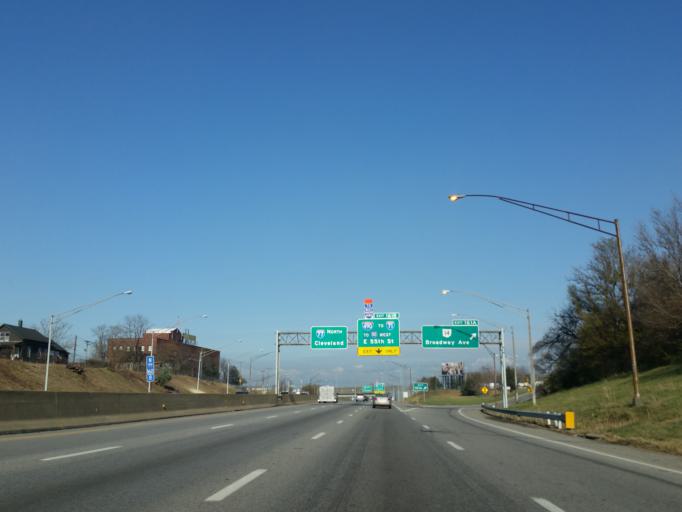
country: US
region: Ohio
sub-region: Cuyahoga County
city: Newburgh Heights
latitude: 41.4717
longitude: -81.6598
